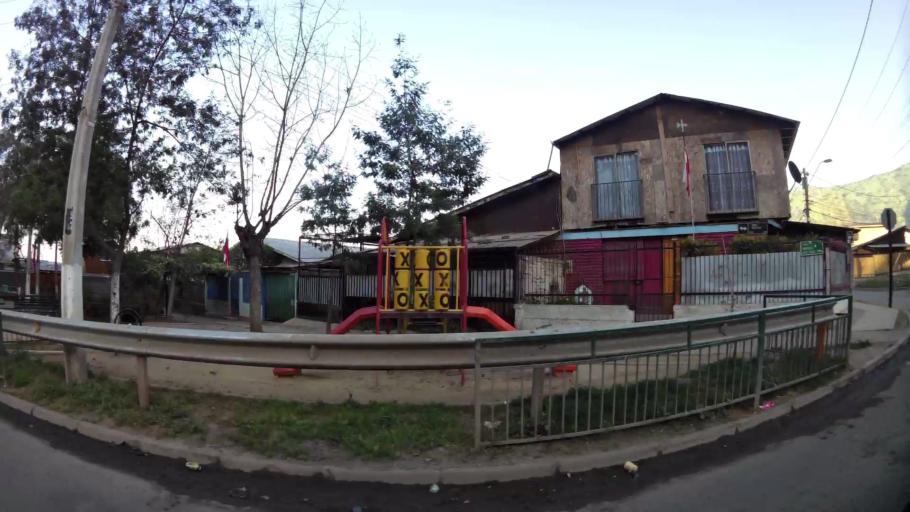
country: CL
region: Santiago Metropolitan
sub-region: Provincia de Chacabuco
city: Chicureo Abajo
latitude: -33.3668
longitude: -70.6291
